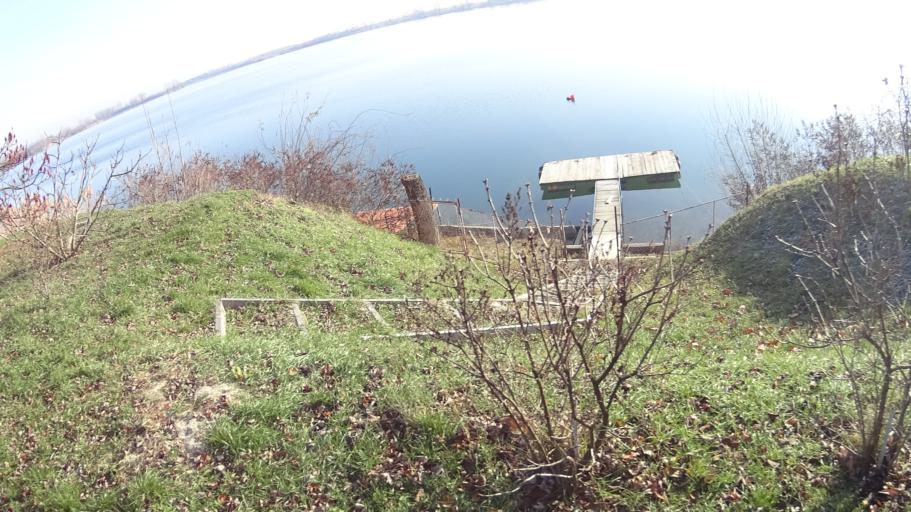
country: HU
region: Borsod-Abauj-Zemplen
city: Nyekladhaza
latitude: 47.9881
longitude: 20.8579
